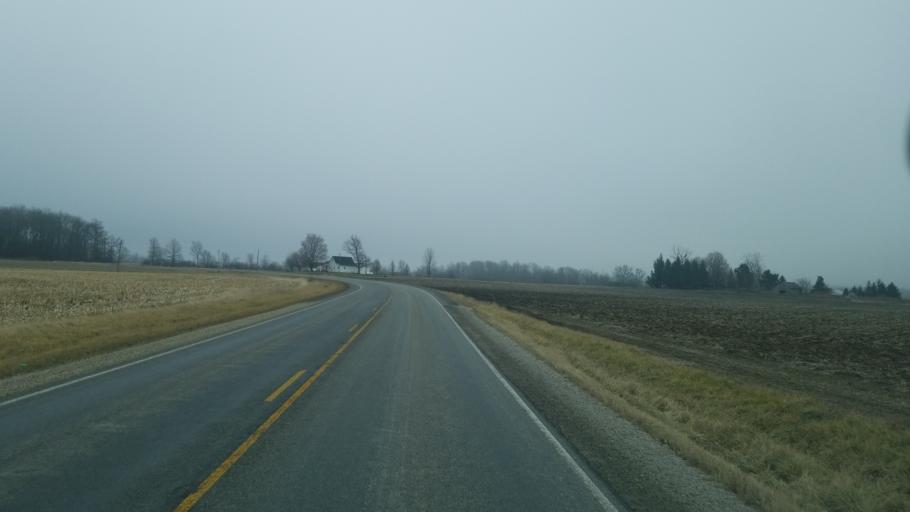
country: US
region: Indiana
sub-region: Adams County
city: Geneva
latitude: 40.5419
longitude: -84.9940
